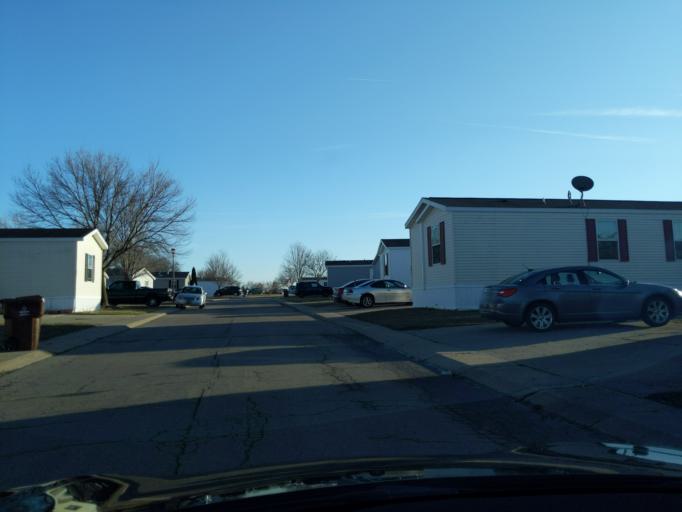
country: US
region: Michigan
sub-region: Jackson County
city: Jackson
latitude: 42.2812
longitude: -84.4728
